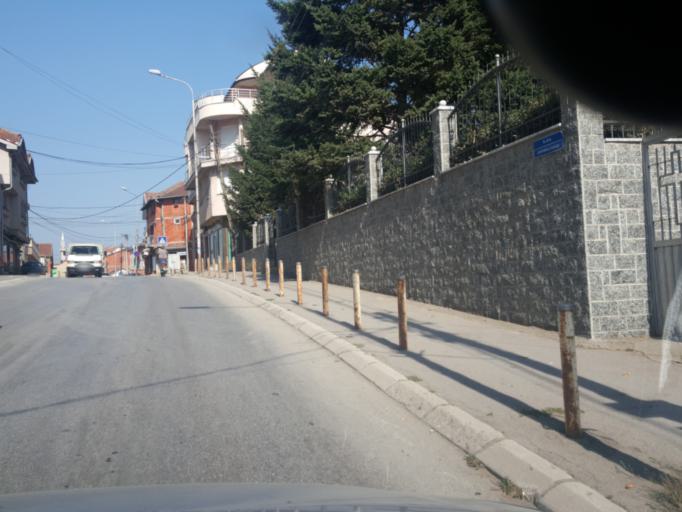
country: XK
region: Gjakova
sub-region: Komuna e Gjakoves
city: Gjakove
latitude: 42.3726
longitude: 20.4234
